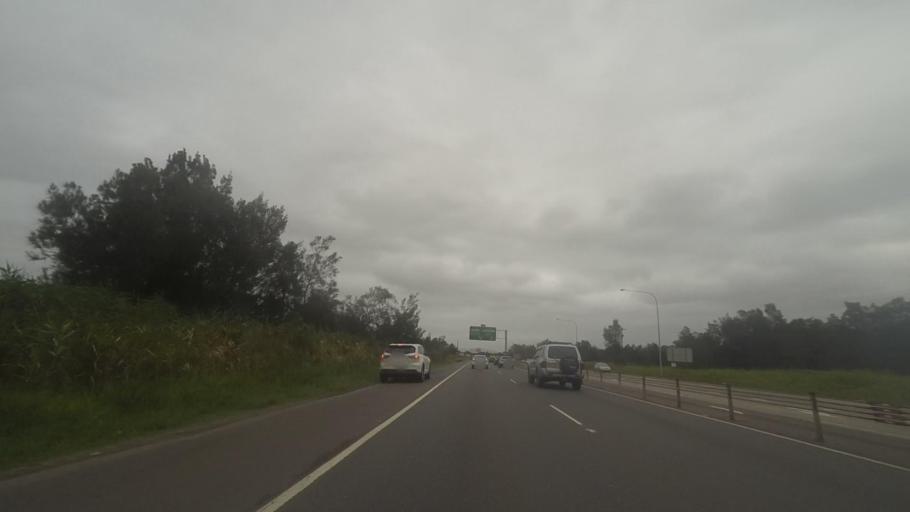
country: AU
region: New South Wales
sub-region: Newcastle
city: Beresfield
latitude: -32.8172
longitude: 151.6950
